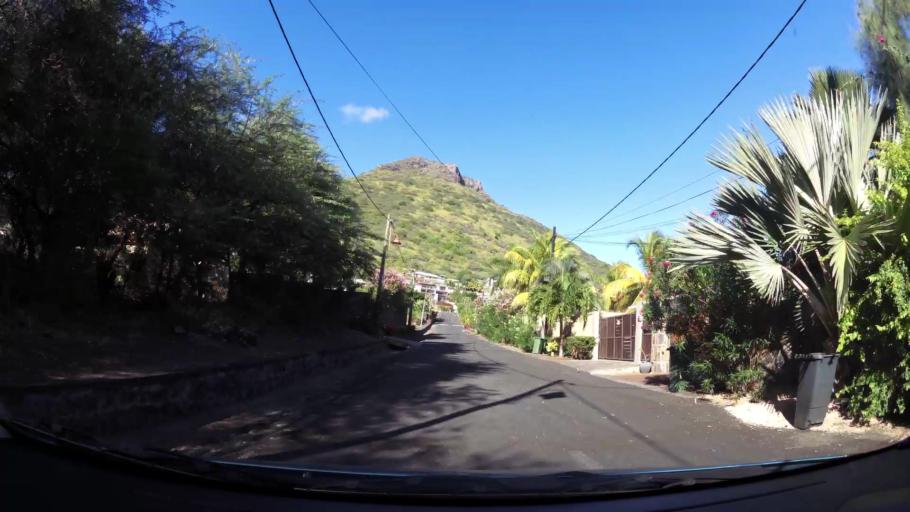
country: MU
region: Black River
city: Tamarin
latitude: -20.3373
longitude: 57.3791
